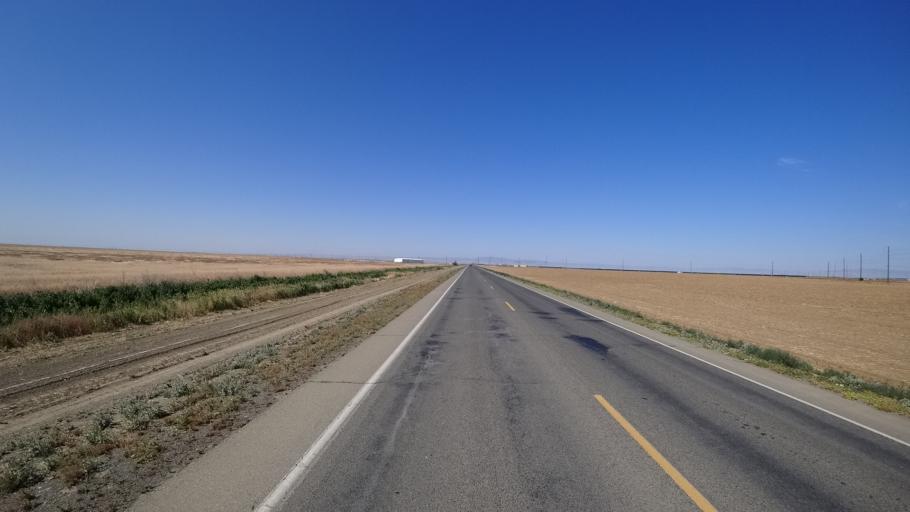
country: US
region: California
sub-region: Kings County
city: Lemoore Station
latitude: 36.2257
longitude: -119.8989
